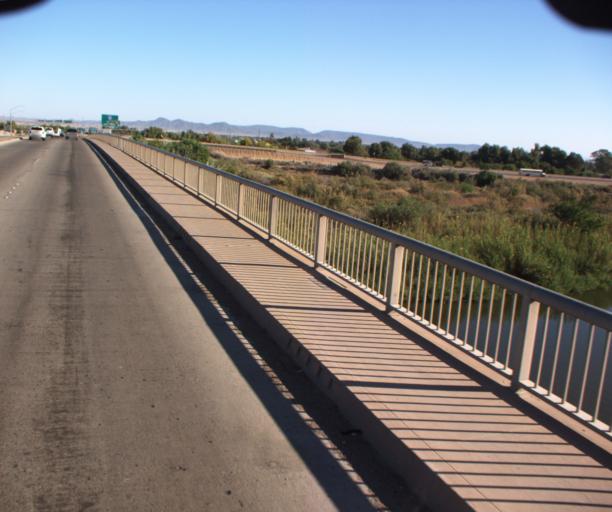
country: US
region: Arizona
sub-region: Yuma County
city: Yuma
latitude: 32.7287
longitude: -114.6245
